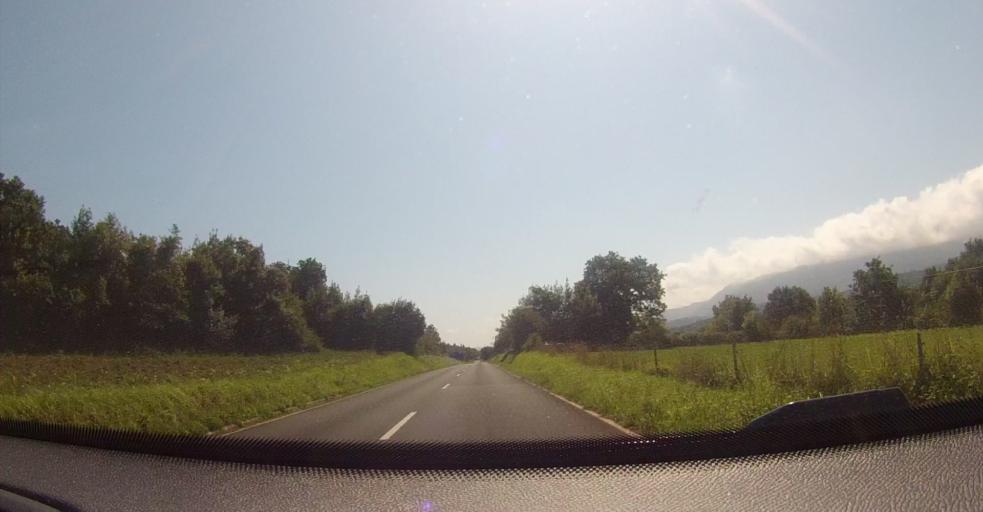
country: ES
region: Asturias
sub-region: Province of Asturias
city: Colunga
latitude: 43.4890
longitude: -5.3059
